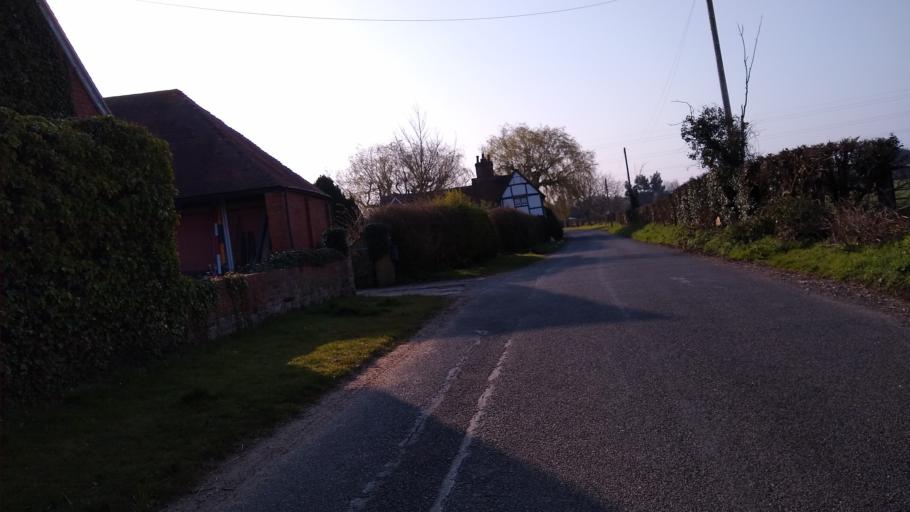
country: GB
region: England
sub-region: Wokingham
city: Winnersh
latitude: 51.4414
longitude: -0.8636
